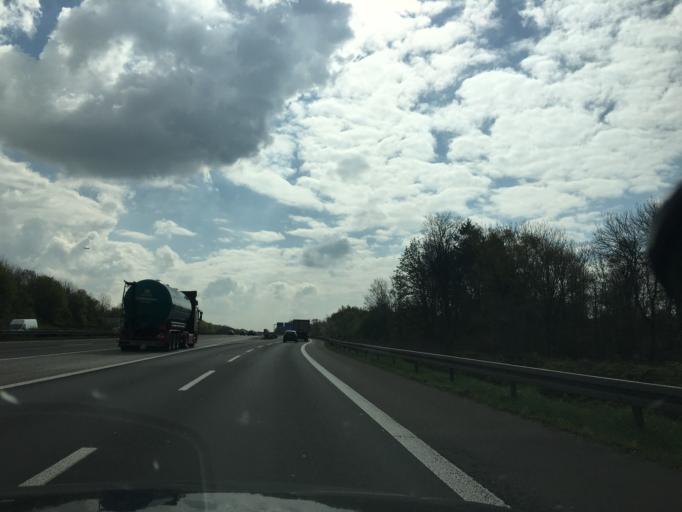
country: DE
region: North Rhine-Westphalia
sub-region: Regierungsbezirk Dusseldorf
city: Ratingen
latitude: 51.3531
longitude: 6.8468
